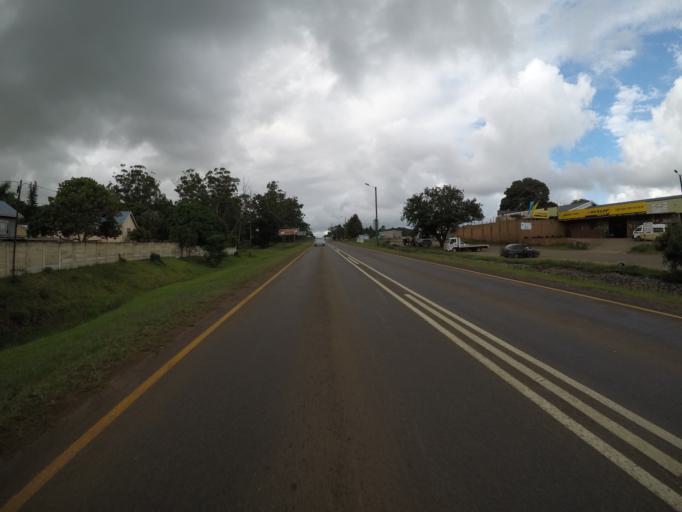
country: ZA
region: KwaZulu-Natal
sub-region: uMkhanyakude District Municipality
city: Mtubatuba
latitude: -28.4121
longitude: 32.1841
